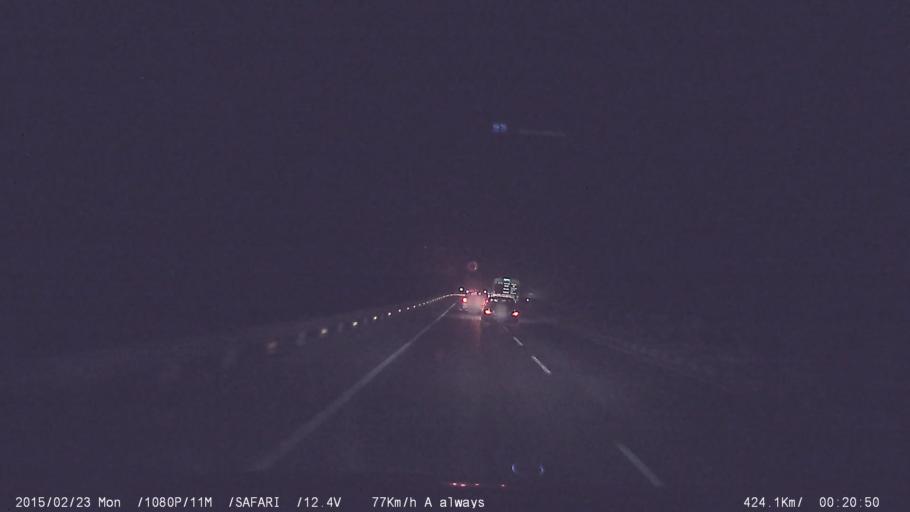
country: IN
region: Tamil Nadu
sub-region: Salem
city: Omalur
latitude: 11.8959
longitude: 78.0656
